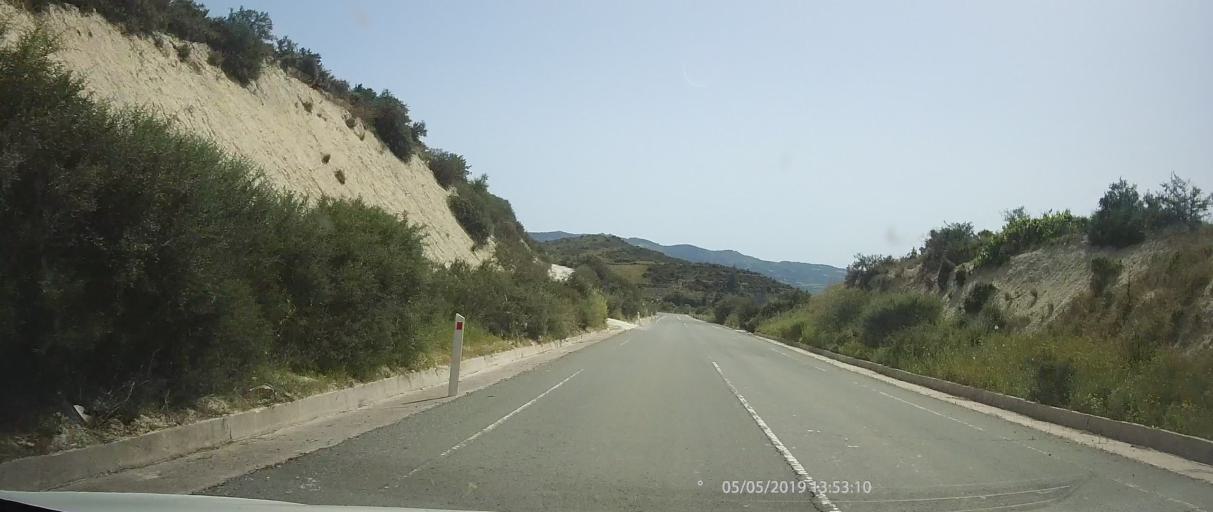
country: CY
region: Limassol
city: Pachna
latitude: 34.8243
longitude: 32.7254
